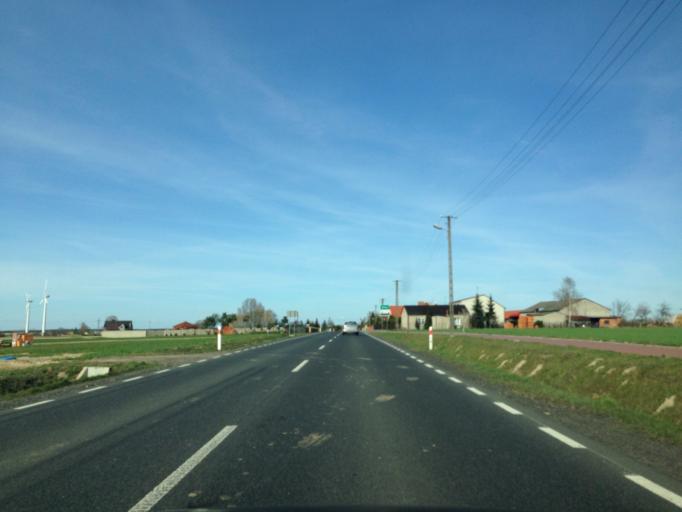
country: PL
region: Lodz Voivodeship
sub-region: Powiat poddebicki
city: Wartkowice
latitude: 51.9779
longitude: 19.0244
